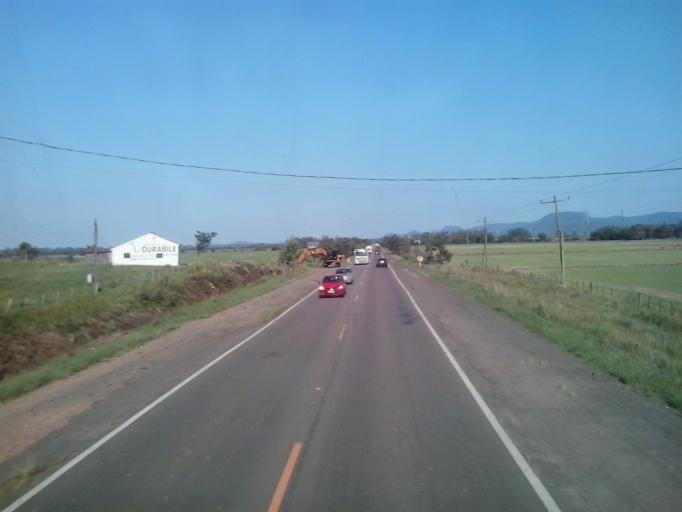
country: BR
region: Rio Grande do Sul
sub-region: Santa Maria
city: Santa Maria
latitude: -29.7183
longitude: -53.6184
